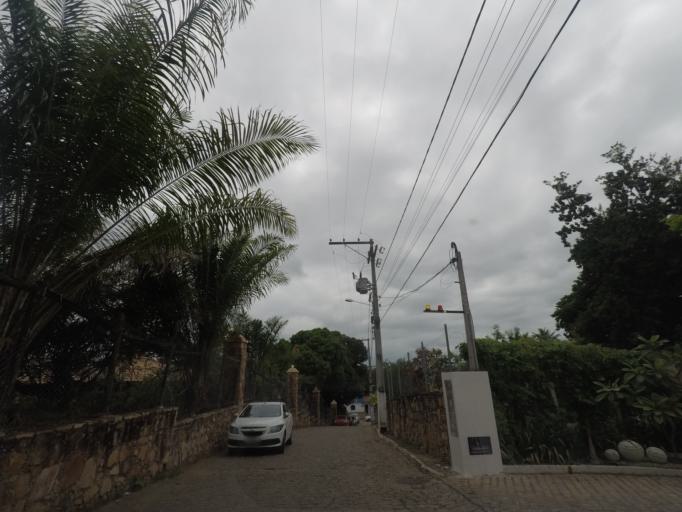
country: BR
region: Bahia
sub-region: Andarai
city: Vera Cruz
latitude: -12.5653
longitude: -41.3943
